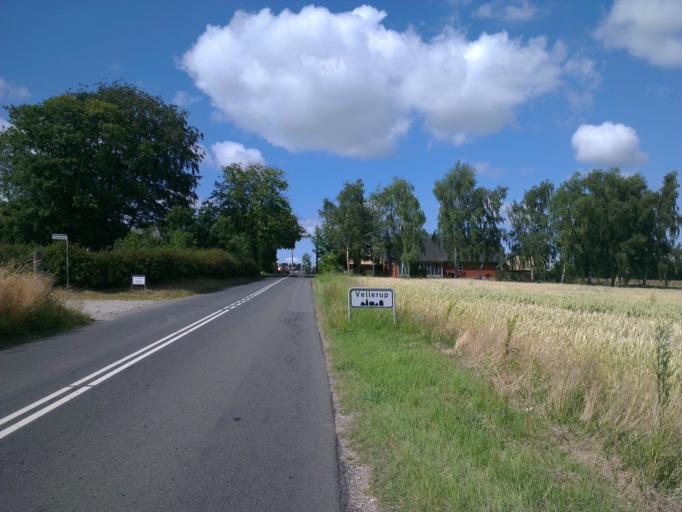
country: DK
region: Zealand
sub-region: Lejre Kommune
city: Ejby
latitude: 55.7419
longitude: 11.8818
